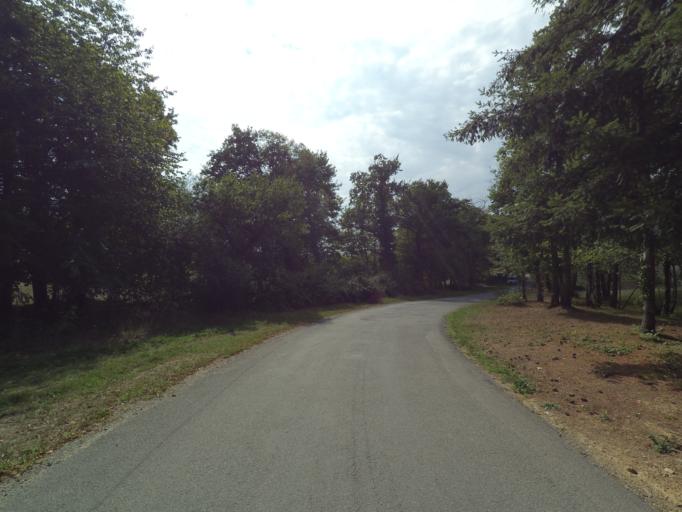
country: FR
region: Poitou-Charentes
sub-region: Departement de la Charente
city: Etagnac
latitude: 45.8469
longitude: 0.7744
